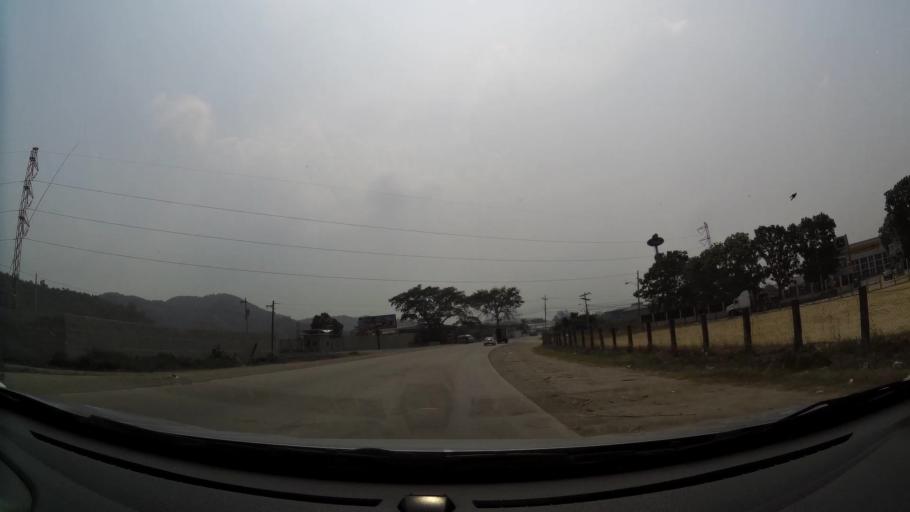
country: HN
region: Cortes
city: Chotepe
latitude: 15.4629
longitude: -87.9657
